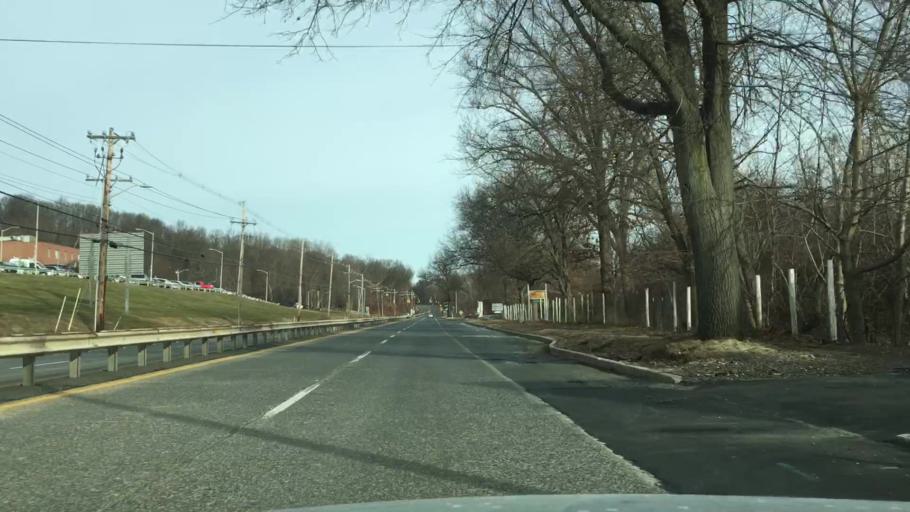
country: US
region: Massachusetts
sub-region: Hampden County
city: Chicopee
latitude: 42.1650
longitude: -72.6328
